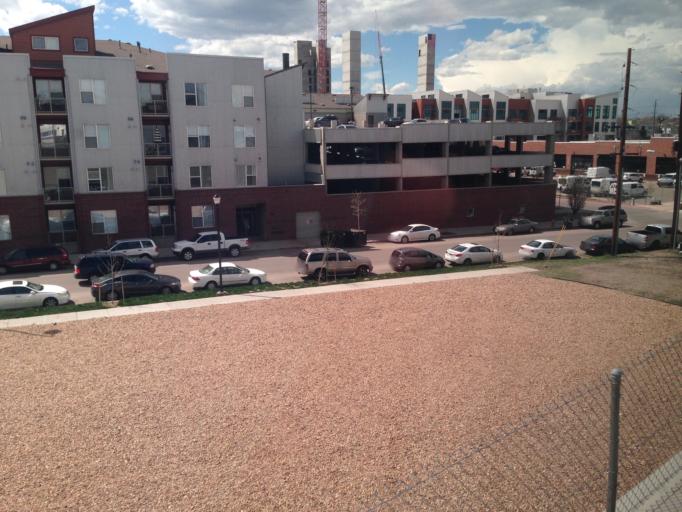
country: US
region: Colorado
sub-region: Denver County
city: Denver
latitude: 39.7602
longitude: -104.9950
